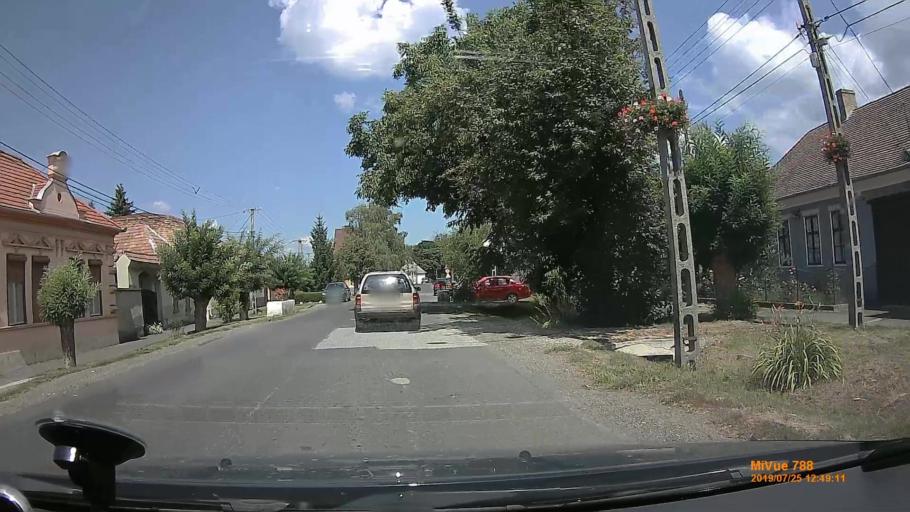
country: HU
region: Borsod-Abauj-Zemplen
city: Abaujszanto
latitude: 48.2736
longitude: 21.1851
